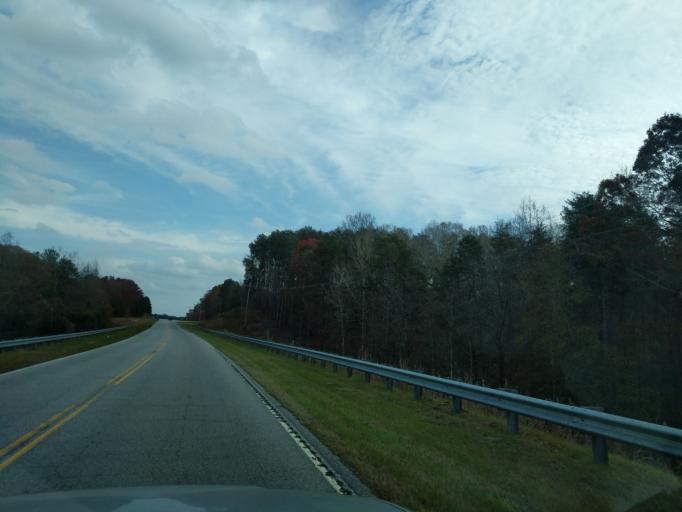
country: US
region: Georgia
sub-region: Franklin County
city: Gumlog
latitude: 34.4985
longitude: -83.0371
